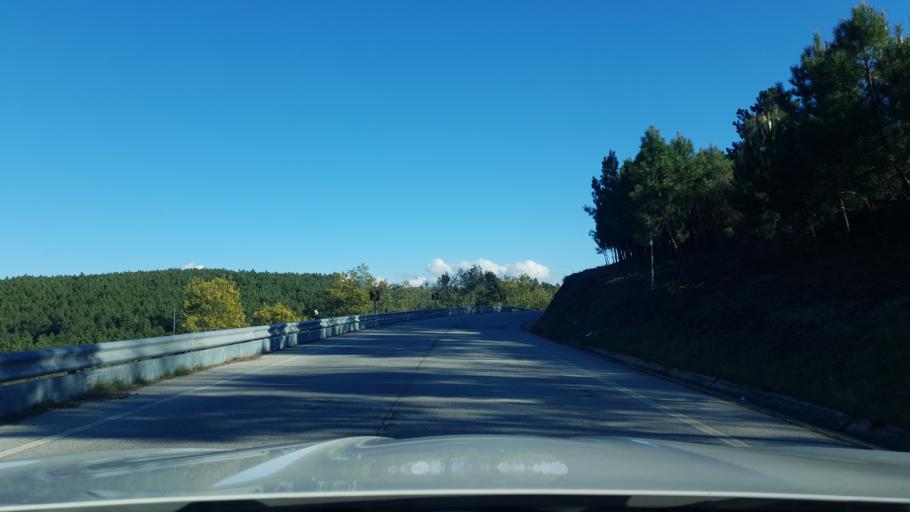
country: PT
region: Braganca
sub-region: Freixo de Espada A Cinta
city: Freixo de Espada a Cinta
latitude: 41.1176
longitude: -6.8199
